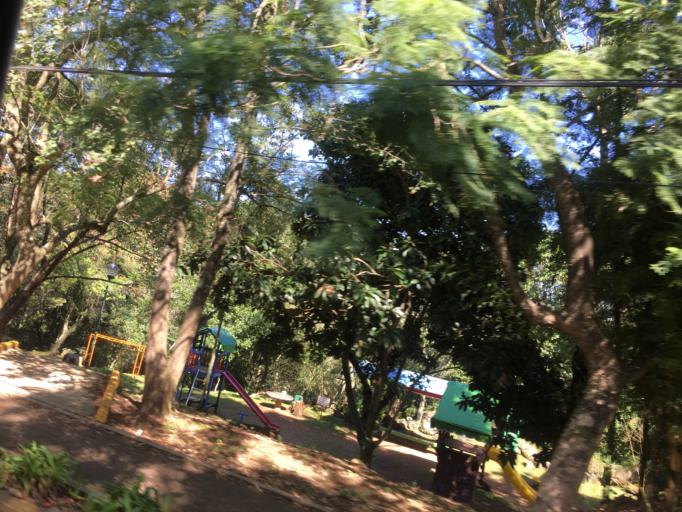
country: MX
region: Veracruz
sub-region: Xalapa
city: Xalapa de Enriquez
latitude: 19.5321
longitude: -96.8930
